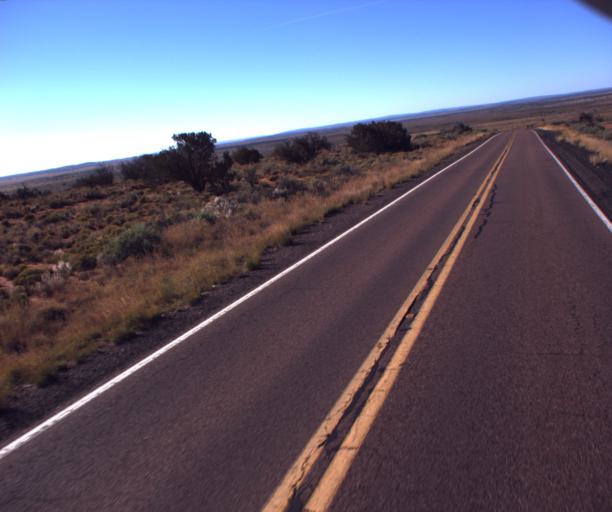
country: US
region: Arizona
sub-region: Navajo County
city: Snowflake
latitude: 34.6389
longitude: -110.3583
